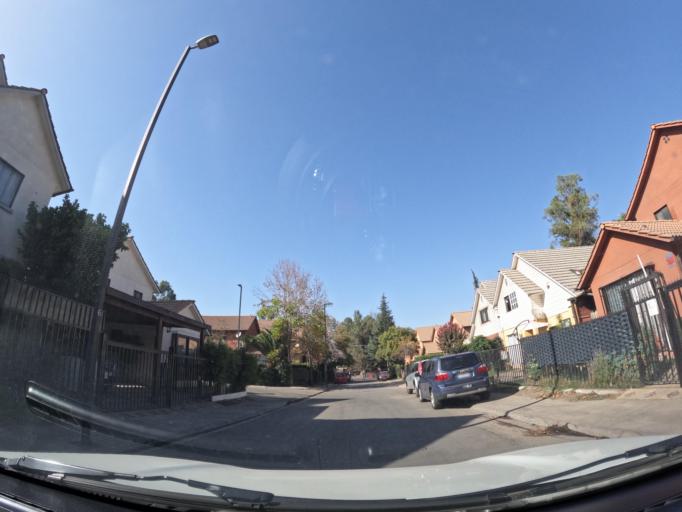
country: CL
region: Santiago Metropolitan
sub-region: Provincia de Santiago
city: Villa Presidente Frei, Nunoa, Santiago, Chile
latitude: -33.5115
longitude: -70.5497
